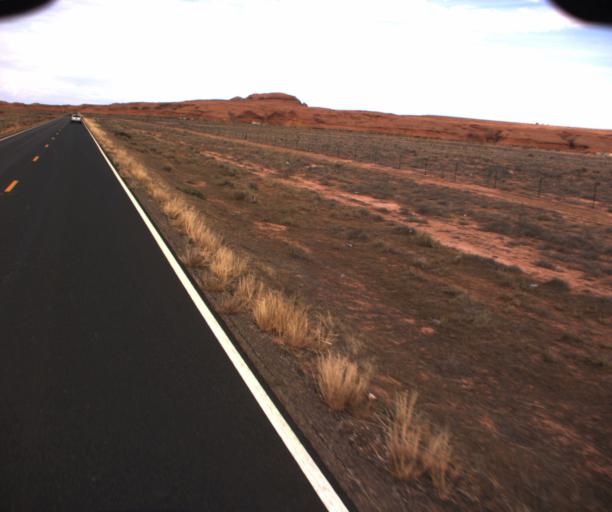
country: US
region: Arizona
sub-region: Apache County
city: Many Farms
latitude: 36.7506
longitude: -109.6433
